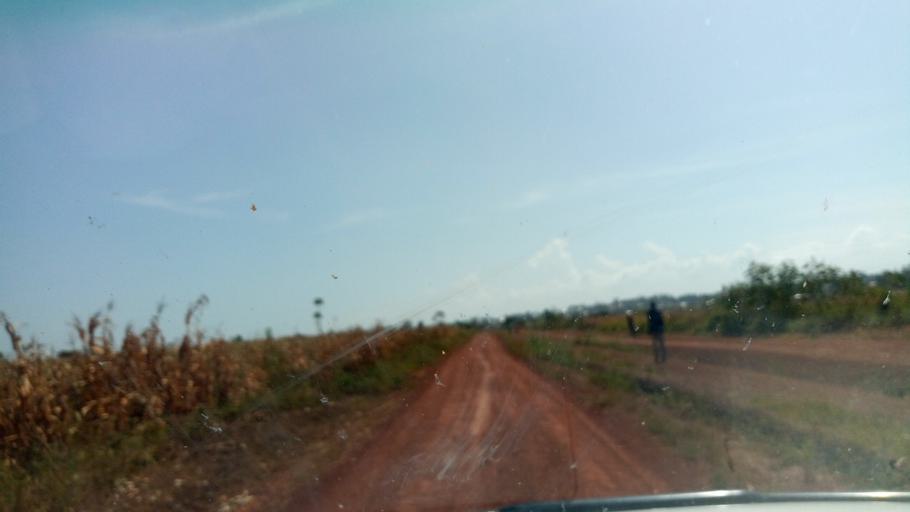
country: UG
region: Western Region
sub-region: Kiryandongo District
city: Kiryandongo
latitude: 1.9501
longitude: 32.1514
